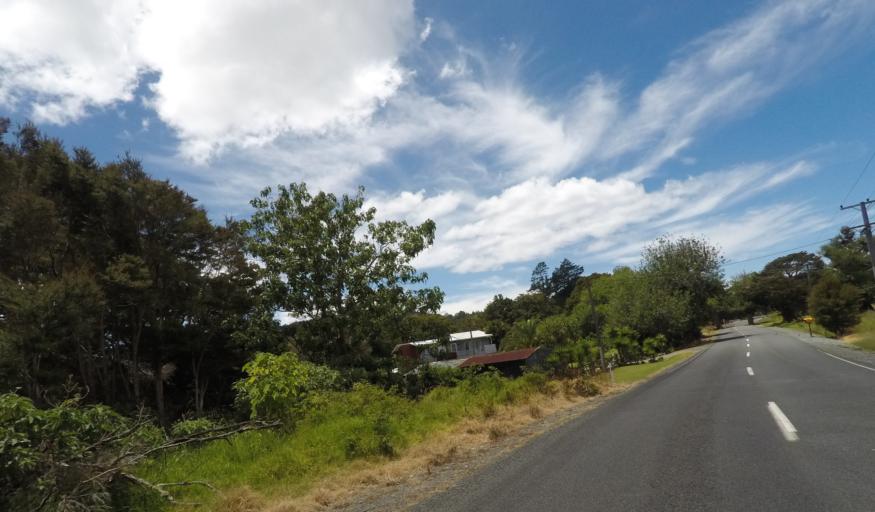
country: NZ
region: Northland
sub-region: Whangarei
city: Ngunguru
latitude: -35.5044
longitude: 174.4282
